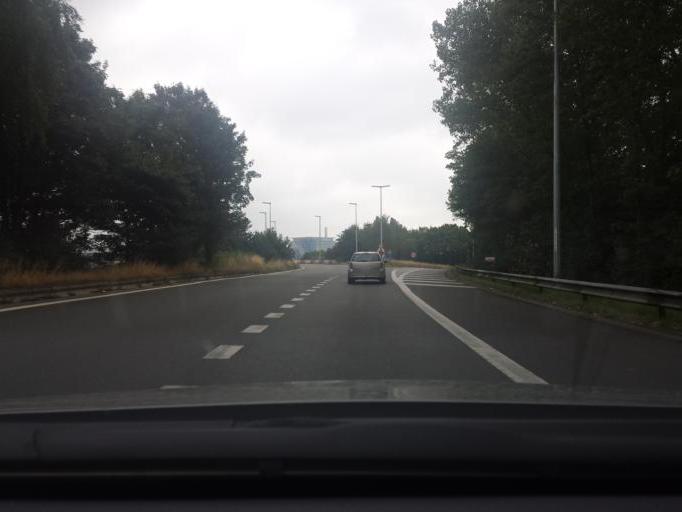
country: BE
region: Flanders
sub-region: Provincie Oost-Vlaanderen
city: Merelbeke
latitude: 51.0092
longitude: 3.7265
